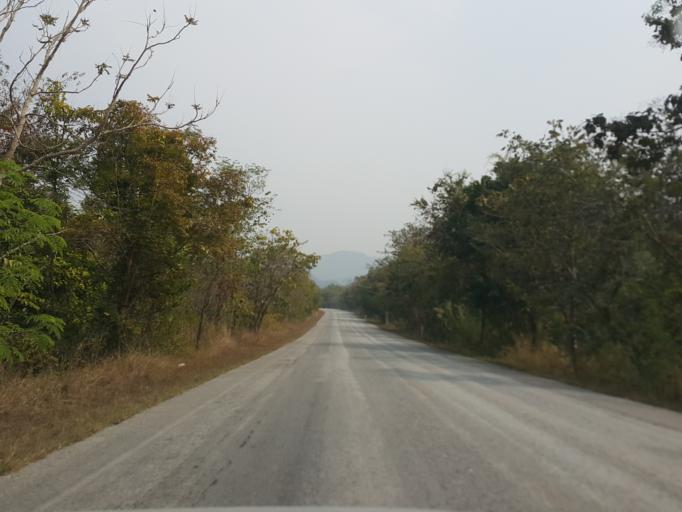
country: TH
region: Lampang
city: Thoen
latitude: 17.6301
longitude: 99.2639
